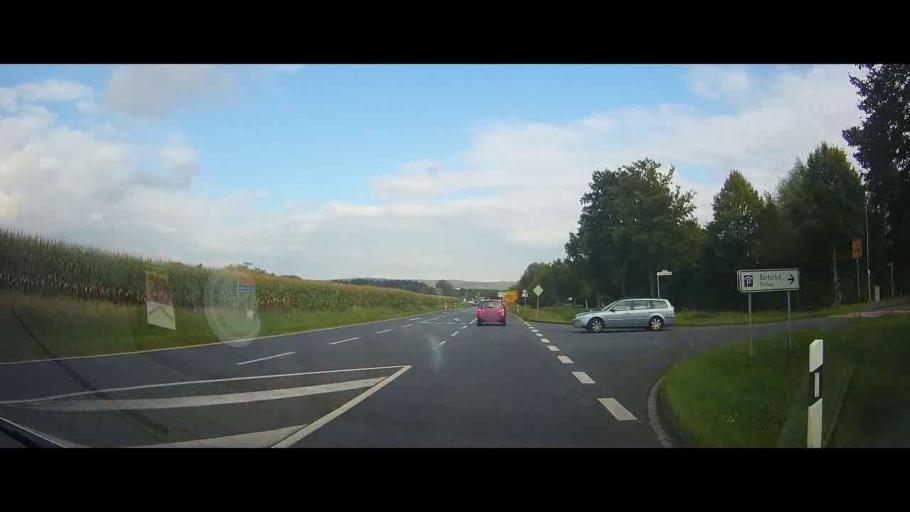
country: DE
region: Lower Saxony
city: Goettingen
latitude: 51.5543
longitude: 9.8847
